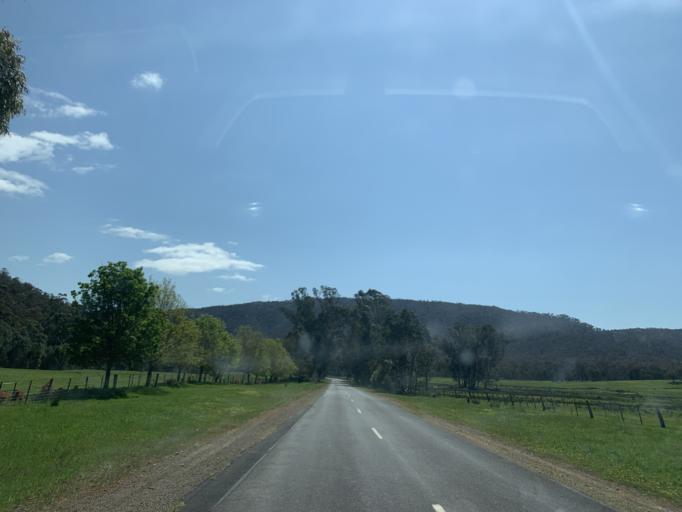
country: AU
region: Victoria
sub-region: Benalla
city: Benalla
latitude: -36.7750
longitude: 146.1380
